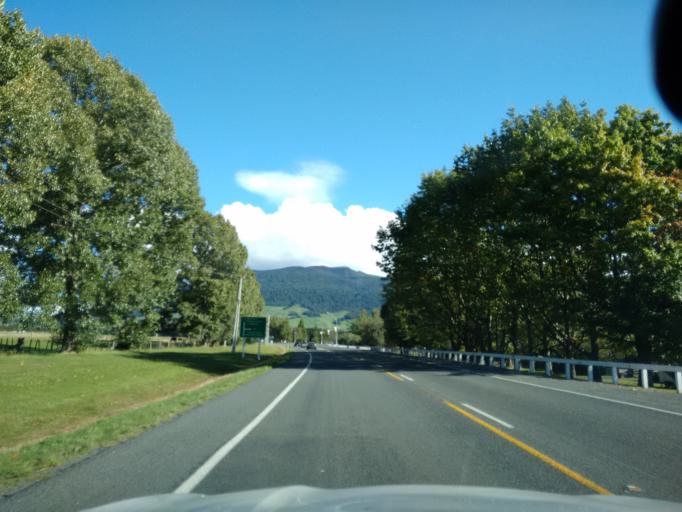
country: NZ
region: Waikato
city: Turangi
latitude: -38.9943
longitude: 175.8062
